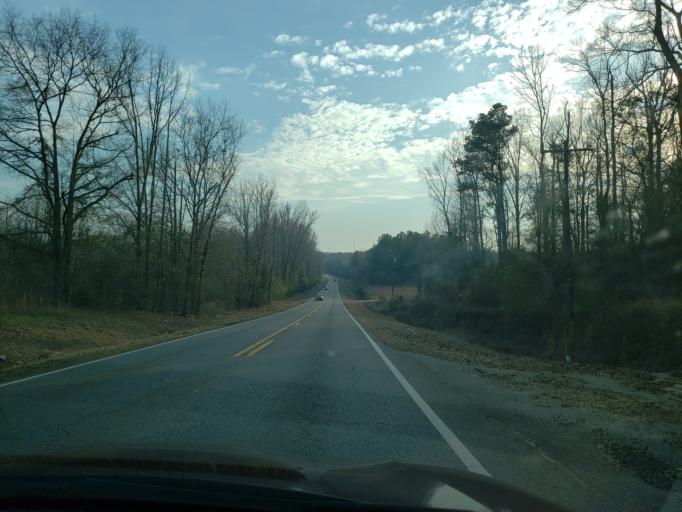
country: US
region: Alabama
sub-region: Hale County
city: Moundville
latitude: 32.9358
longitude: -87.6308
